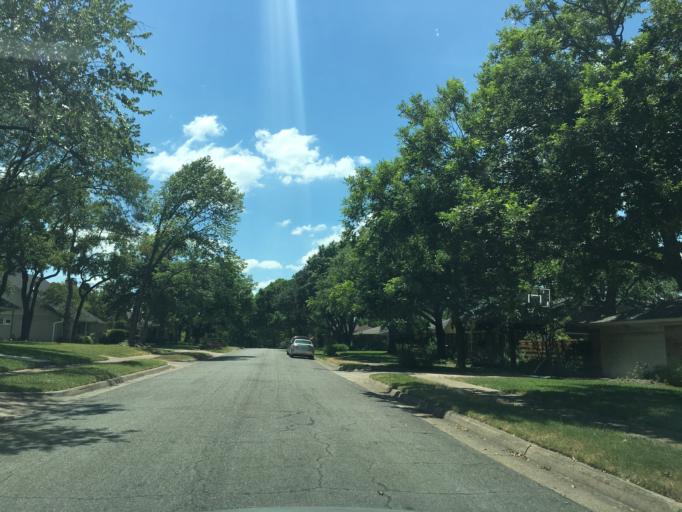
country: US
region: Texas
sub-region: Dallas County
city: Garland
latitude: 32.8489
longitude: -96.6946
